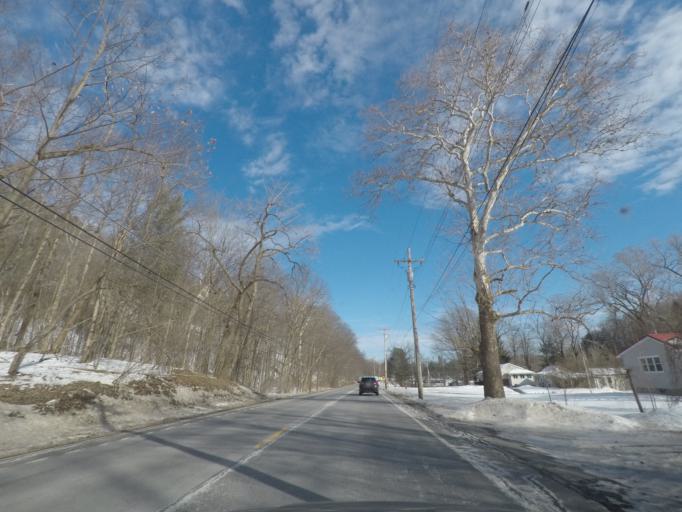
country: US
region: New York
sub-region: Albany County
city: Altamont
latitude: 42.7790
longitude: -74.0619
